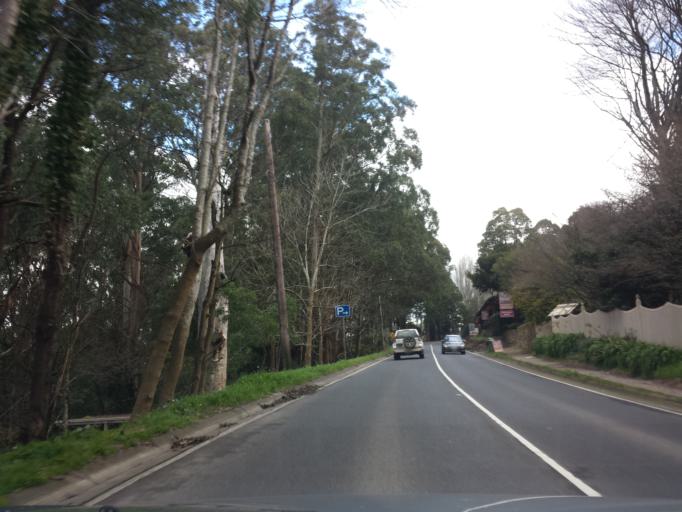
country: AU
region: Victoria
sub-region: Yarra Ranges
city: Kallista
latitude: -37.8670
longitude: 145.3530
